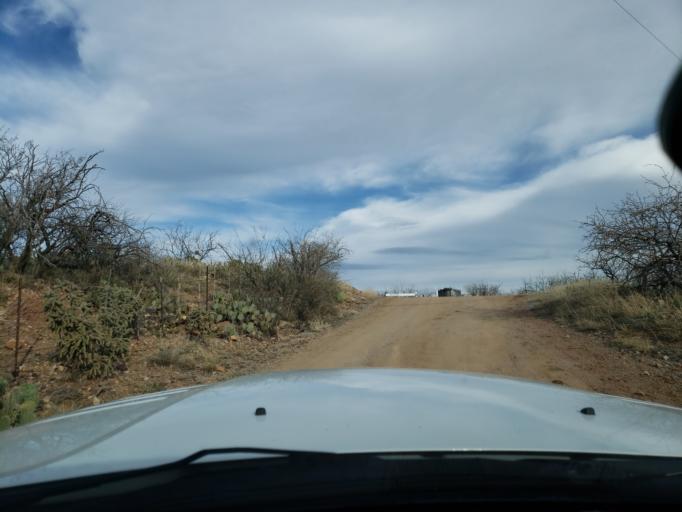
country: US
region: Arizona
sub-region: Pinal County
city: San Manuel
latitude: 32.5483
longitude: -110.7051
